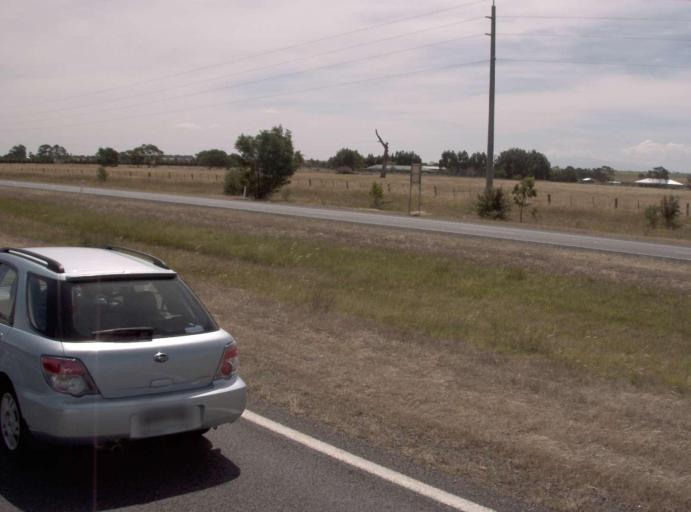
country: AU
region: Victoria
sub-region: Wellington
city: Heyfield
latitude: -38.1354
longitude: 146.8016
